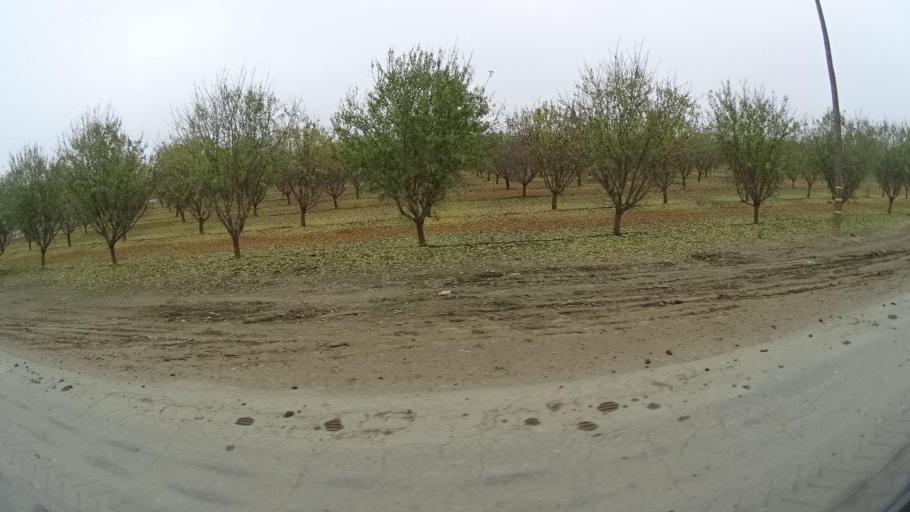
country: US
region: California
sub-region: Kern County
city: Wasco
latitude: 35.7169
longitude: -119.4194
